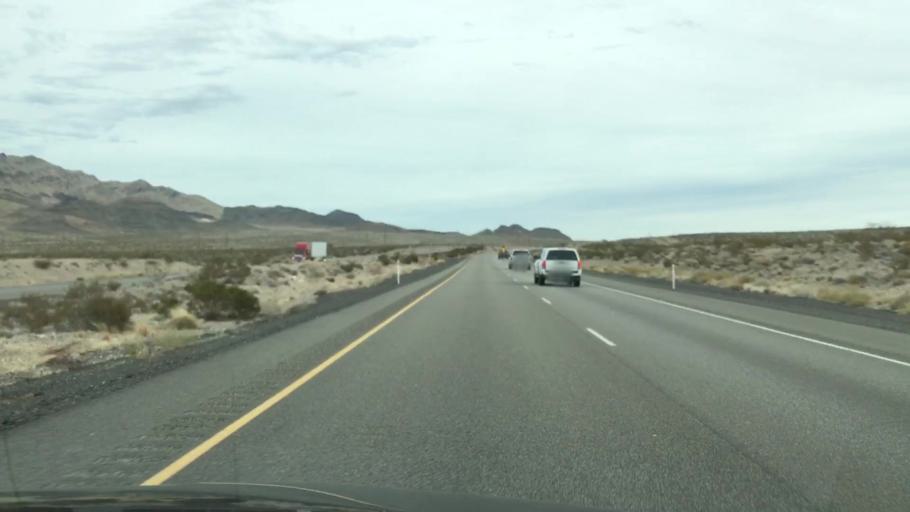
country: US
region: Nevada
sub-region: Nye County
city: Pahrump
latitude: 36.6001
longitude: -115.9831
